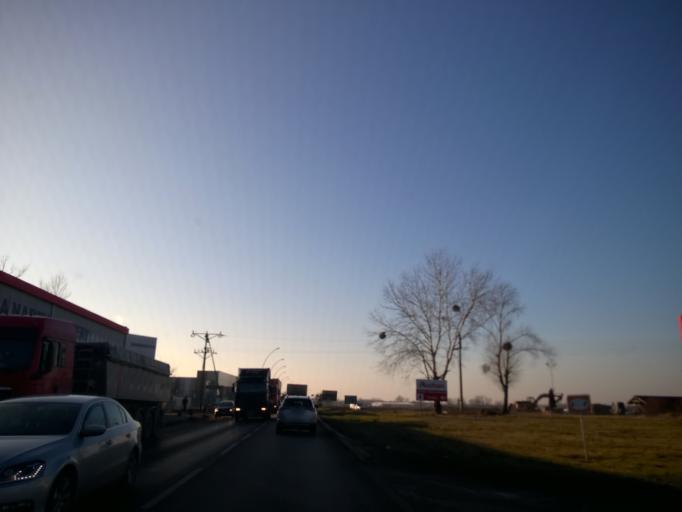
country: PL
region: Lower Silesian Voivodeship
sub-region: Powiat wroclawski
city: Bielany Wroclawskie
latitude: 51.0779
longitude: 16.9542
